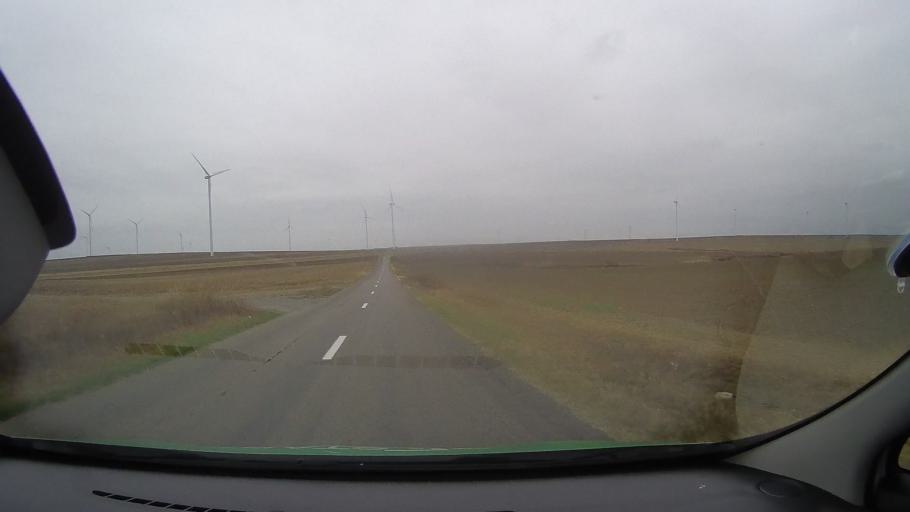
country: RO
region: Constanta
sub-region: Comuna Pantelimon
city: Pantelimon
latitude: 44.5135
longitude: 28.3343
